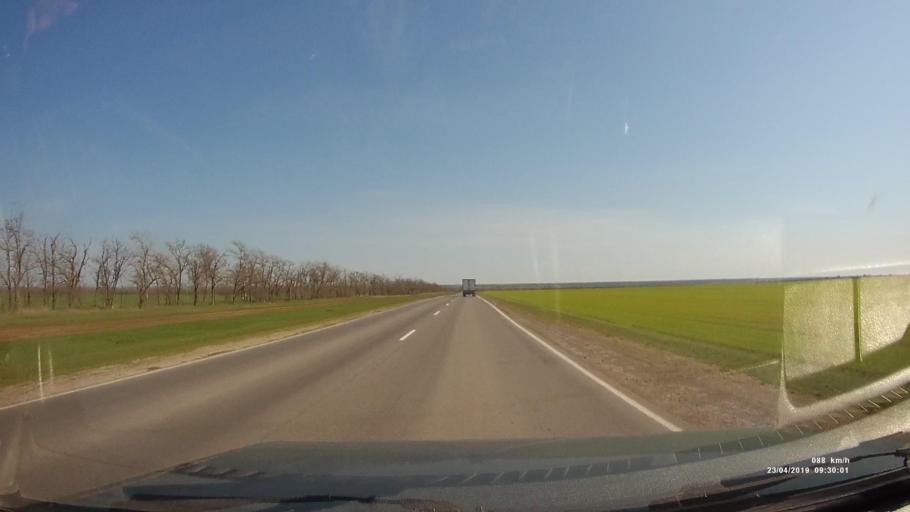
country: RU
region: Rostov
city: Gundorovskiy
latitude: 46.7667
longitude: 41.8114
